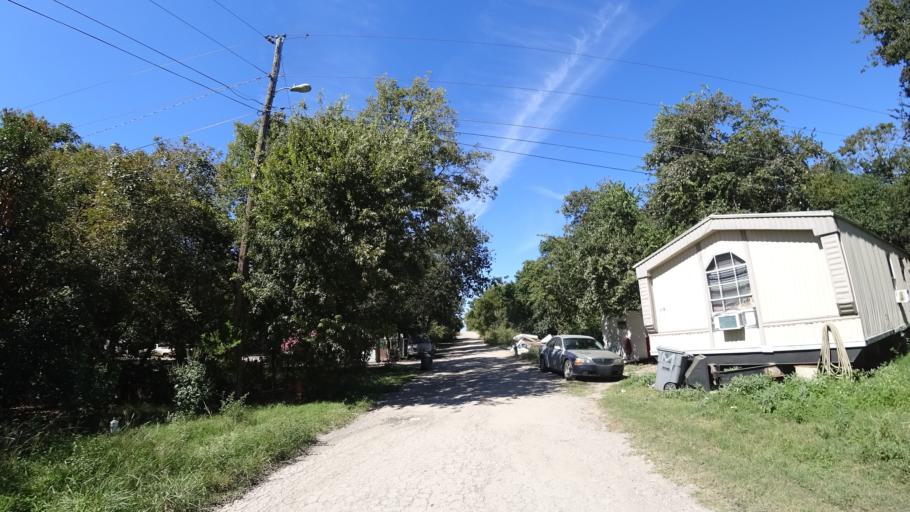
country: US
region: Texas
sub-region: Travis County
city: Austin
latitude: 30.2111
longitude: -97.6867
